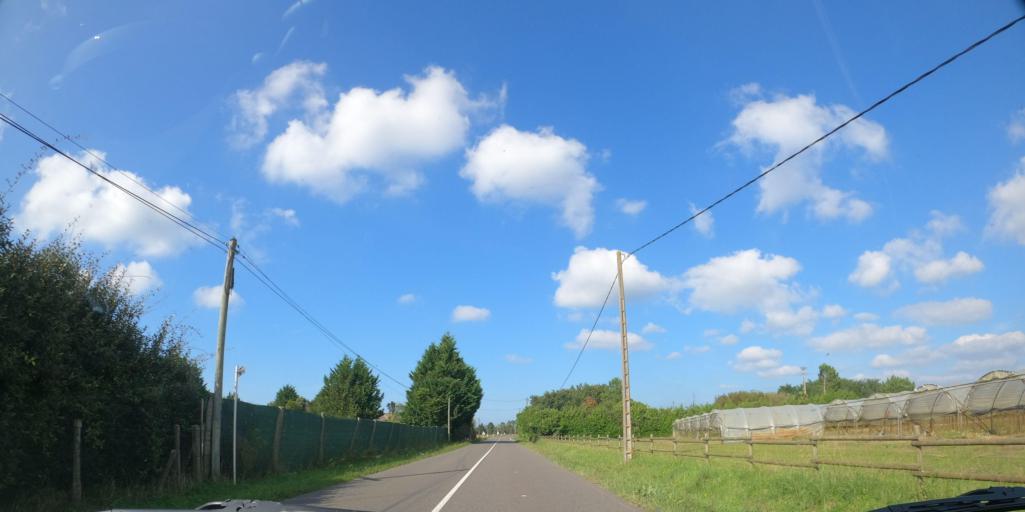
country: FR
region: Aquitaine
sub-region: Departement des Landes
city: Soustons
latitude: 43.7237
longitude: -1.3469
